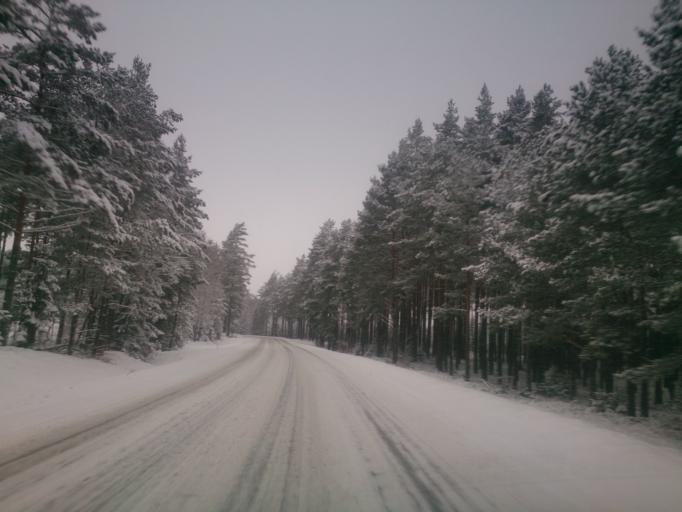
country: SE
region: OEstergoetland
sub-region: Finspangs Kommun
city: Finspang
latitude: 58.6626
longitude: 15.7799
